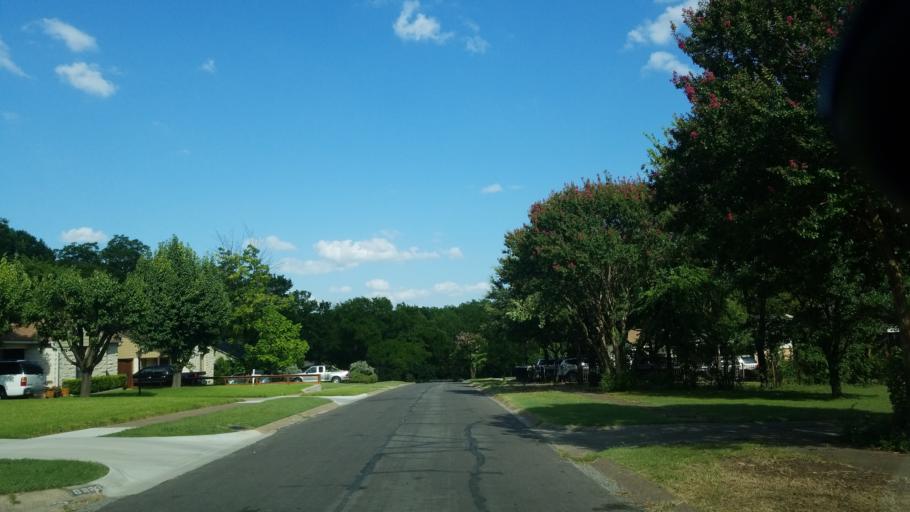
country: US
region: Texas
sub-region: Dallas County
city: Dallas
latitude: 32.7701
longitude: -96.7136
